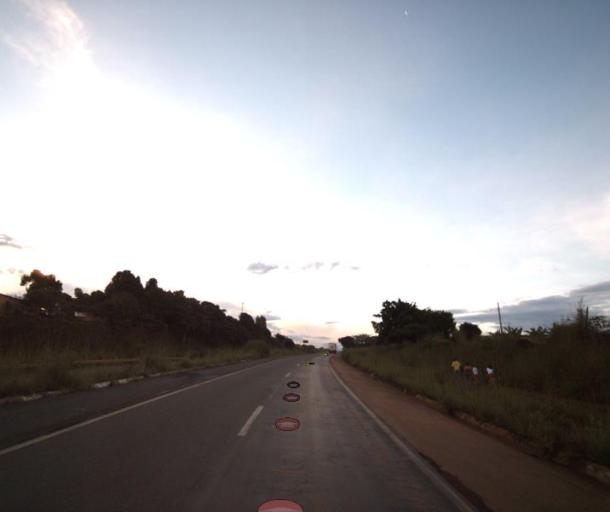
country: BR
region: Goias
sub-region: Anapolis
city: Anapolis
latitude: -16.2678
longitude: -48.9796
